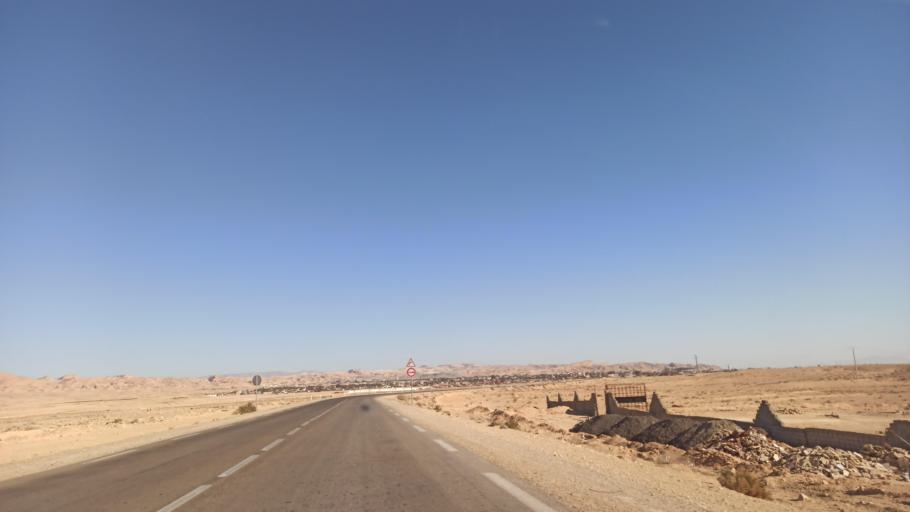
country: TN
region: Gafsa
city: Al Metlaoui
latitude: 34.3043
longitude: 8.3631
